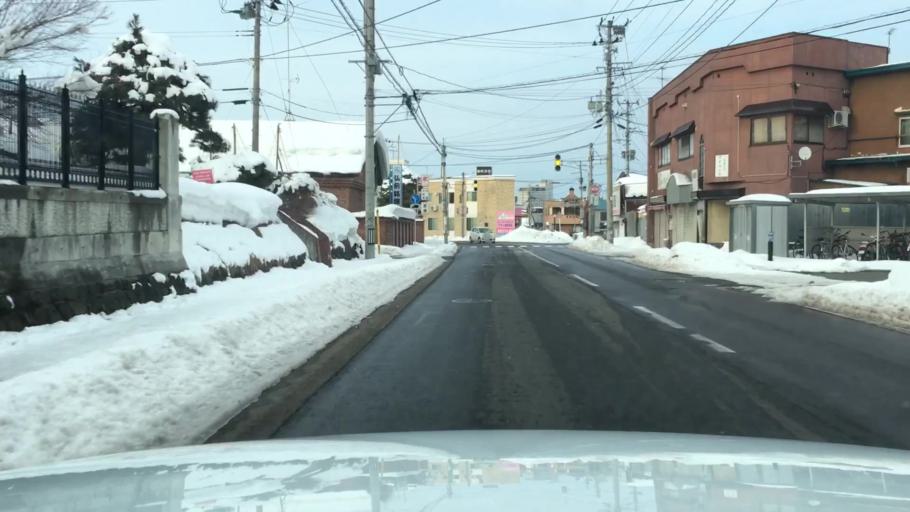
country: JP
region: Aomori
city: Hirosaki
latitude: 40.5903
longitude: 140.4740
